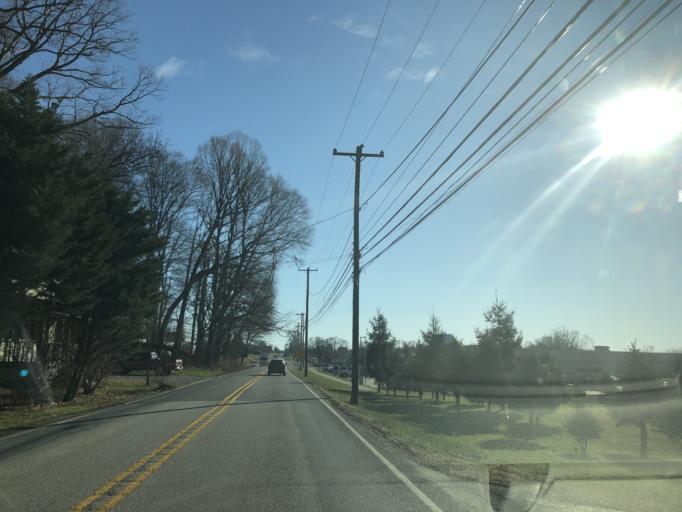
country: US
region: Pennsylvania
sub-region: Chester County
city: Toughkenamon
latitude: 39.8130
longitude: -75.7518
